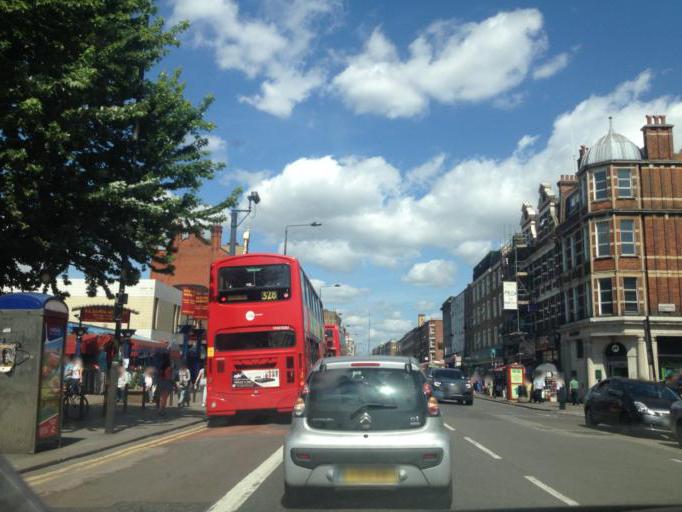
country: GB
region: England
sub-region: Greater London
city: Belsize Park
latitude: 51.5388
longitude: -0.1945
